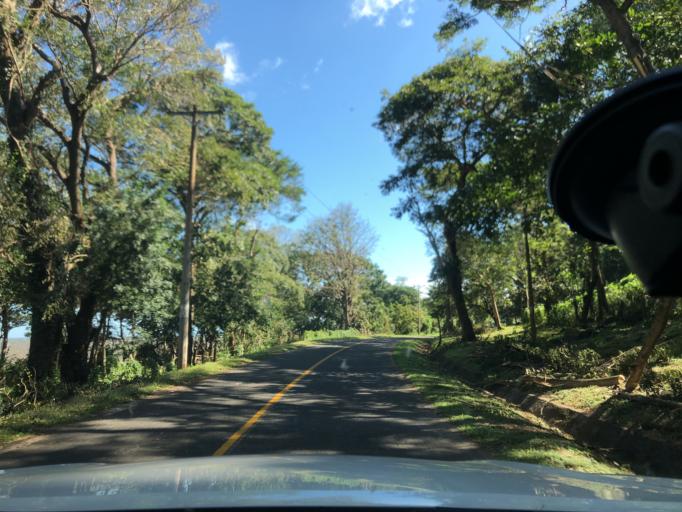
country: NI
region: Rivas
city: Cardenas
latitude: 11.2395
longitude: -85.5727
